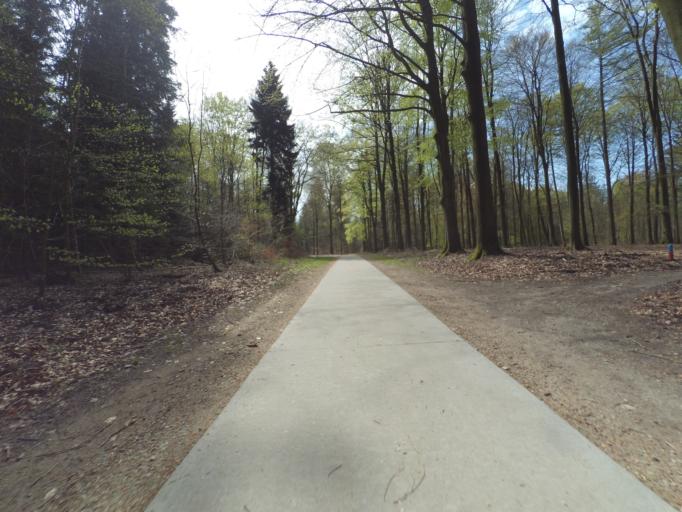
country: NL
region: Gelderland
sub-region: Gemeente Epe
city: Epe
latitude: 52.3777
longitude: 5.9565
